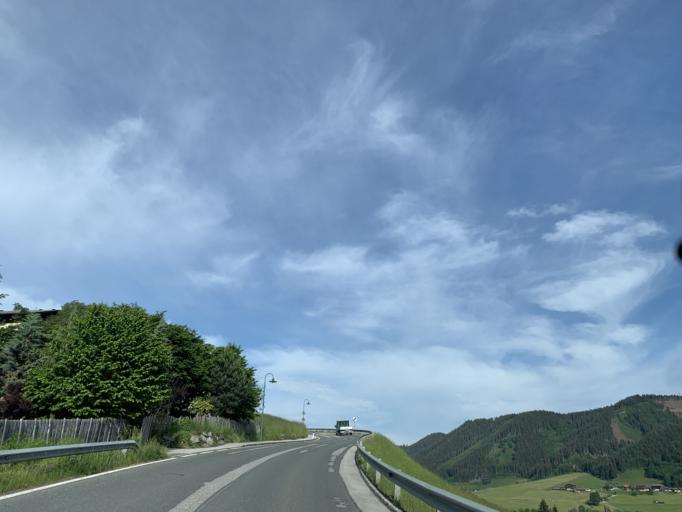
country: AT
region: Styria
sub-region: Politischer Bezirk Liezen
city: Schladming
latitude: 47.3885
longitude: 13.6845
